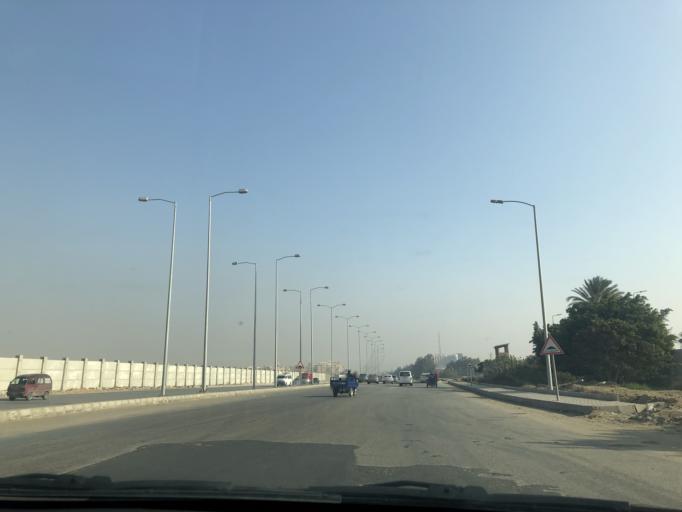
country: EG
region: Al Jizah
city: Madinat Sittah Uktubar
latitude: 29.9556
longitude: 31.0789
